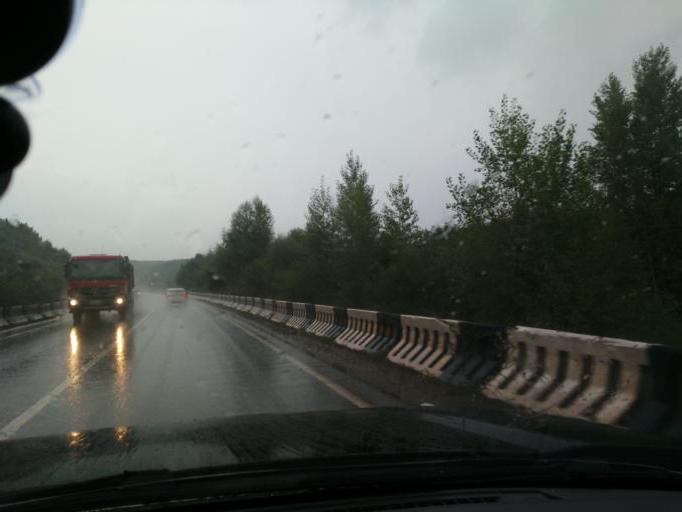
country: RU
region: Perm
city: Osa
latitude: 57.1804
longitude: 55.5759
